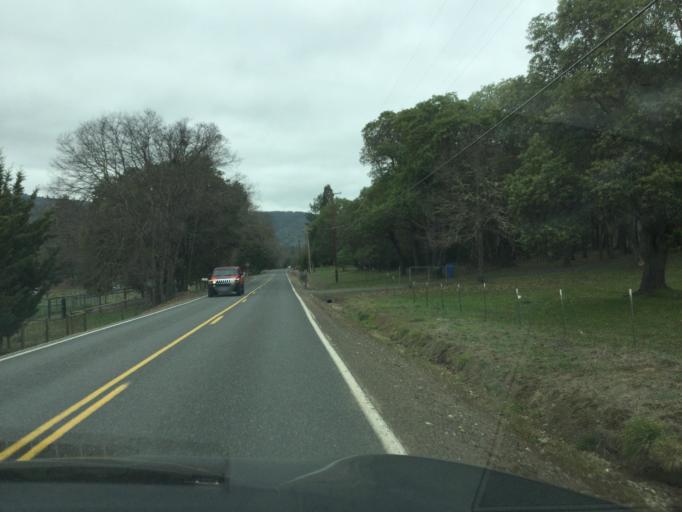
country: US
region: Oregon
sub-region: Jackson County
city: Gold Hill
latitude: 42.3991
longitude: -123.0197
